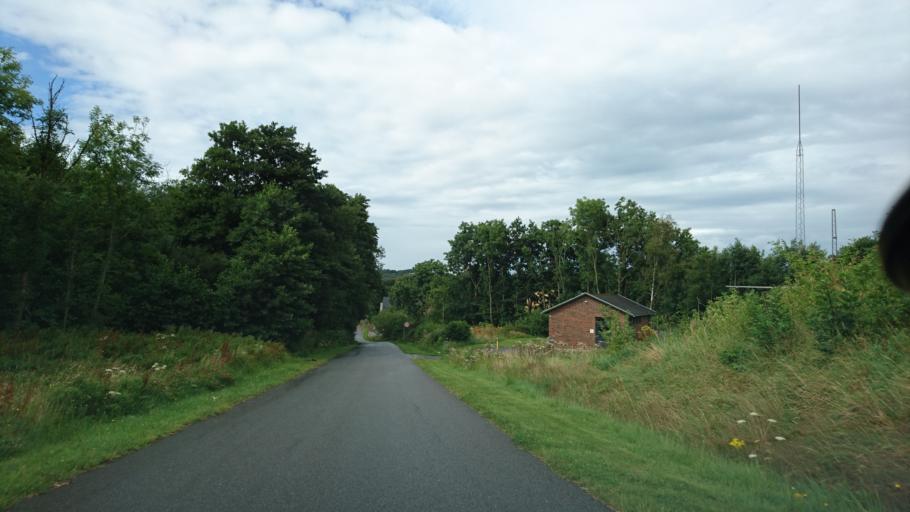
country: DK
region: North Denmark
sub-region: Frederikshavn Kommune
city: Frederikshavn
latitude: 57.3978
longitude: 10.4777
